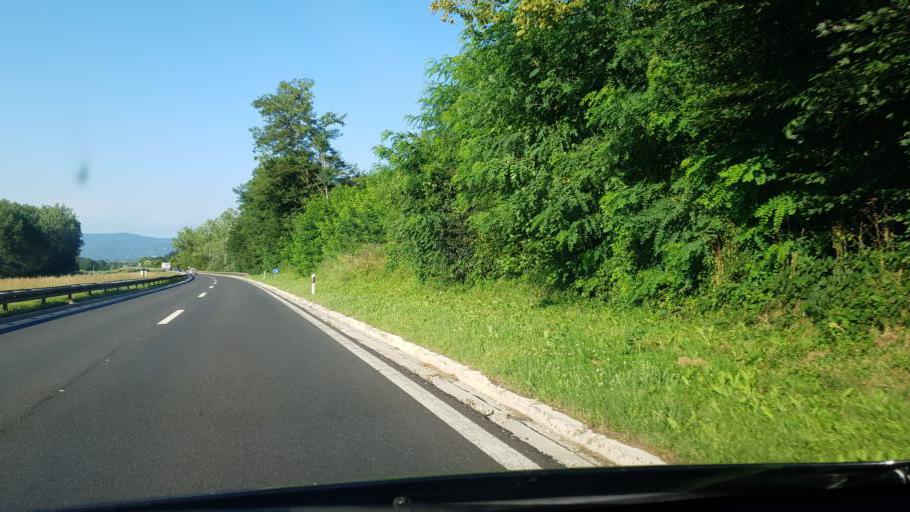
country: HR
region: Istarska
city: Pazin
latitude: 45.2821
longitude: 14.0238
